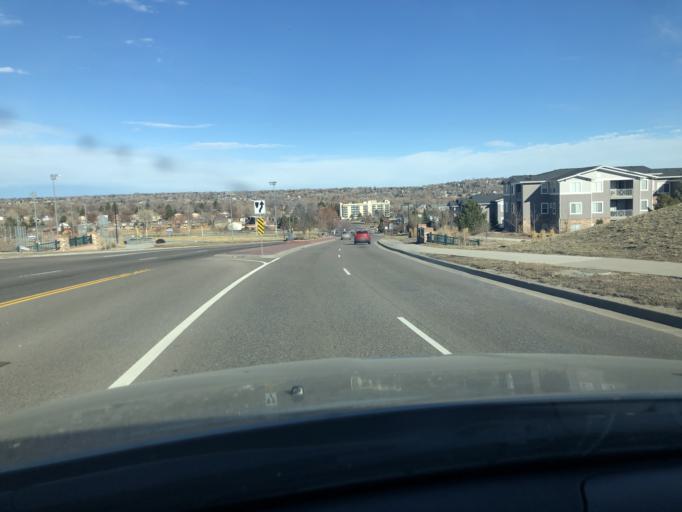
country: US
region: Colorado
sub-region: Jefferson County
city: Arvada
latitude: 39.7979
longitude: -105.1126
